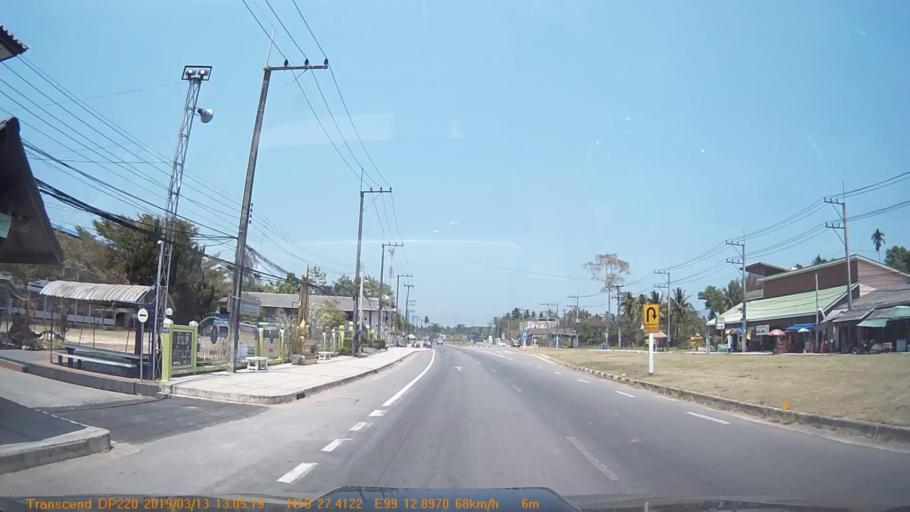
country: TH
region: Chumphon
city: Chumphon
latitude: 10.4572
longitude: 99.2150
